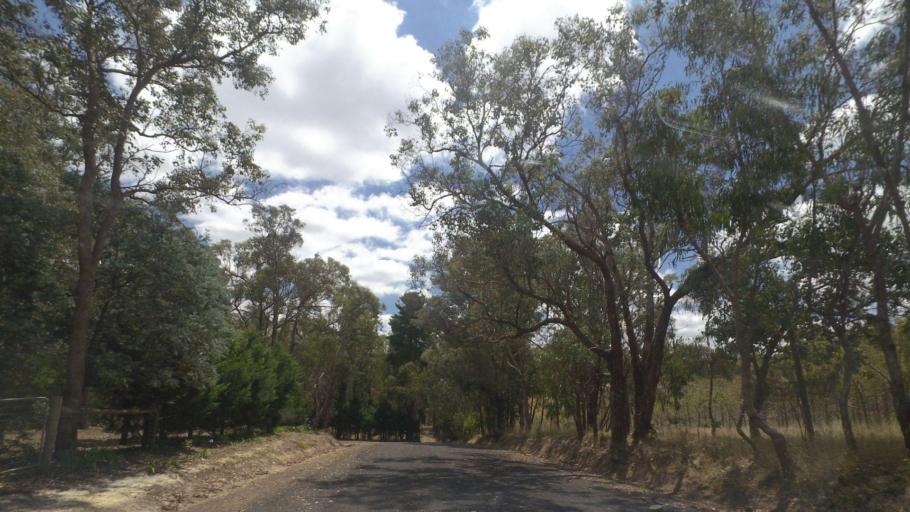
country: AU
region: Victoria
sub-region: Manningham
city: Warrandyte
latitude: -37.7483
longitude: 145.2585
